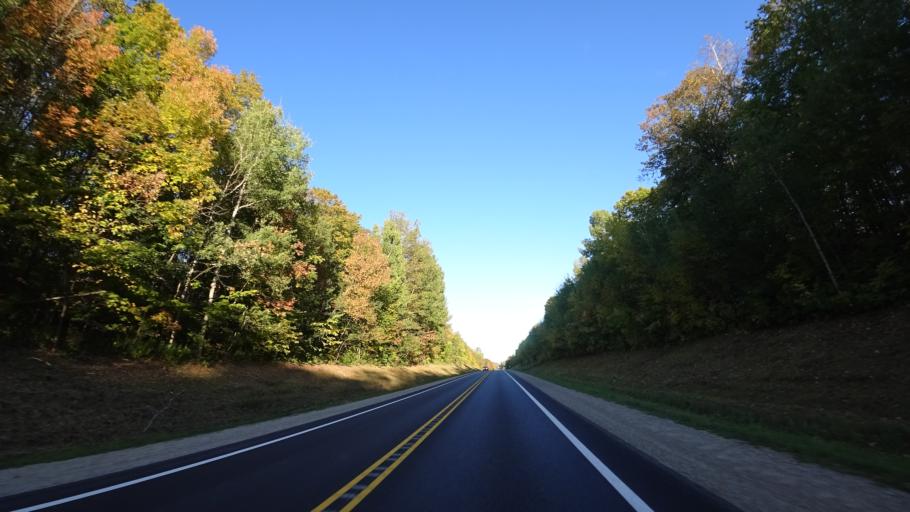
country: US
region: Michigan
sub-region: Luce County
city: Newberry
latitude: 46.3356
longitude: -85.8078
